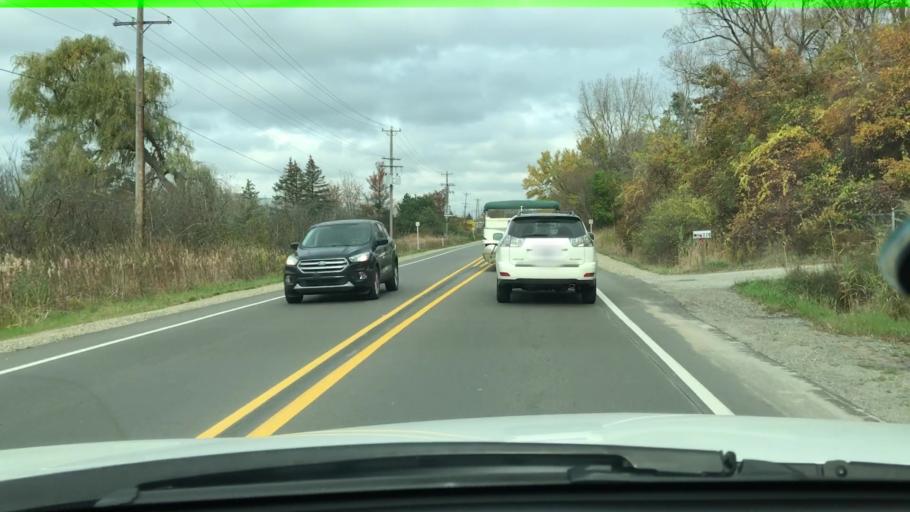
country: US
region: Michigan
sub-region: Oakland County
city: Waterford
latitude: 42.6536
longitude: -83.4437
